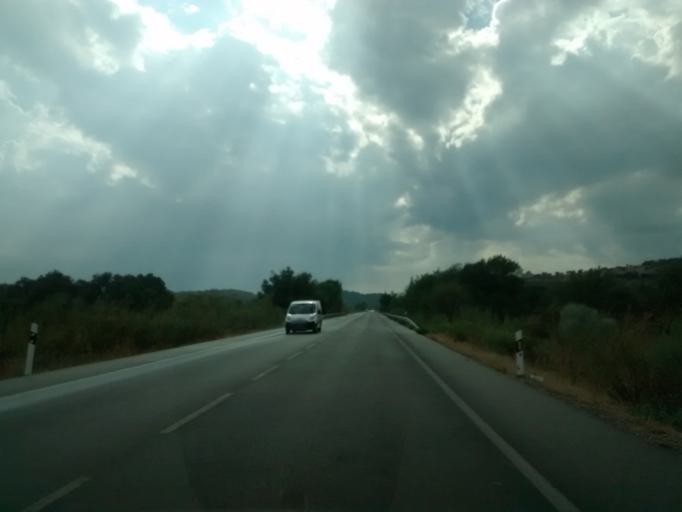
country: ES
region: Andalusia
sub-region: Provincia de Cadiz
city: Prado del Rey
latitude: 36.7527
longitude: -5.5592
